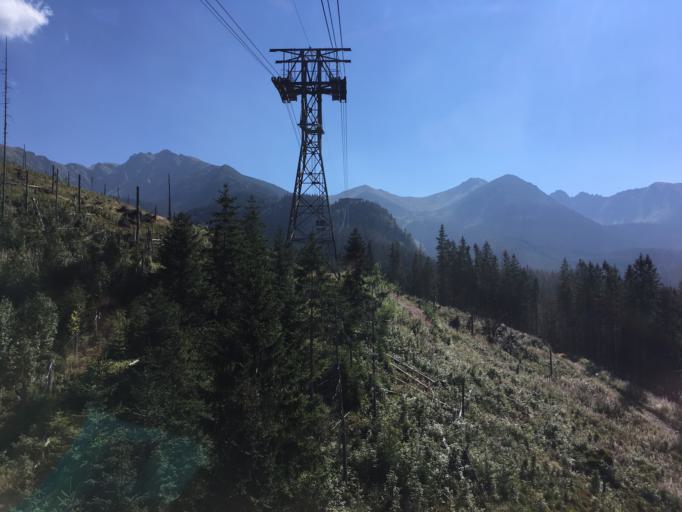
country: PL
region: Lesser Poland Voivodeship
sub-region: Powiat tatrzanski
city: Zakopane
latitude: 49.2614
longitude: 19.9767
